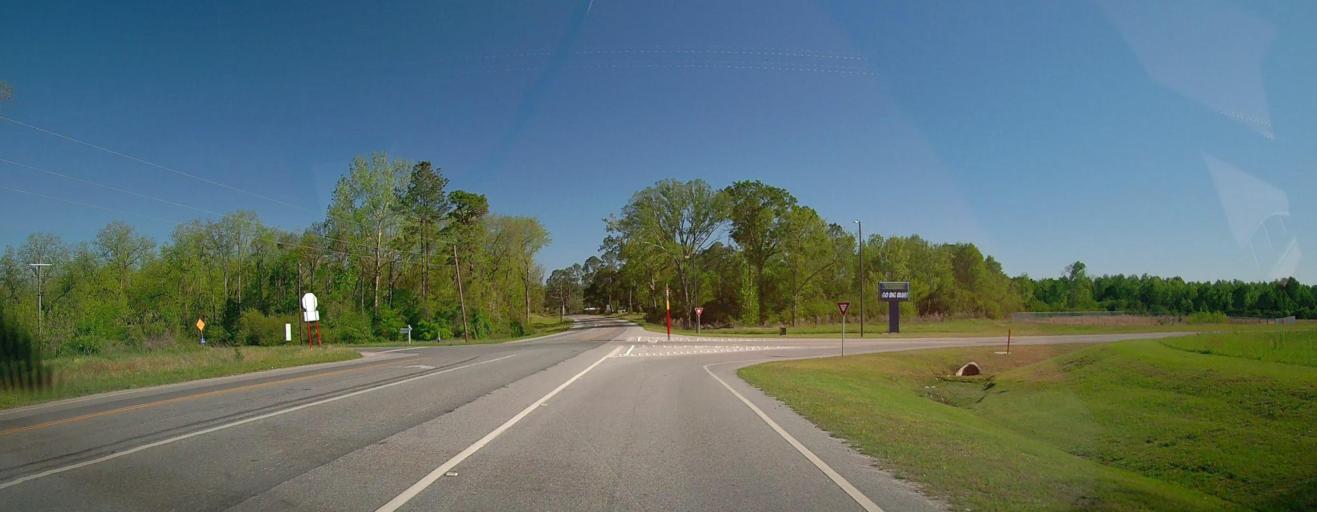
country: US
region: Georgia
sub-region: Wilcox County
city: Rochelle
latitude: 31.9401
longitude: -83.4421
